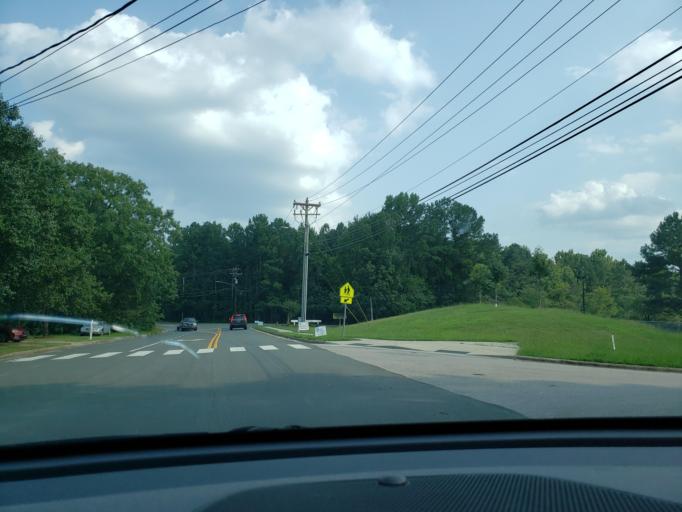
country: US
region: North Carolina
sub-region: Durham County
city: Durham
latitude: 35.9303
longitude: -78.9223
